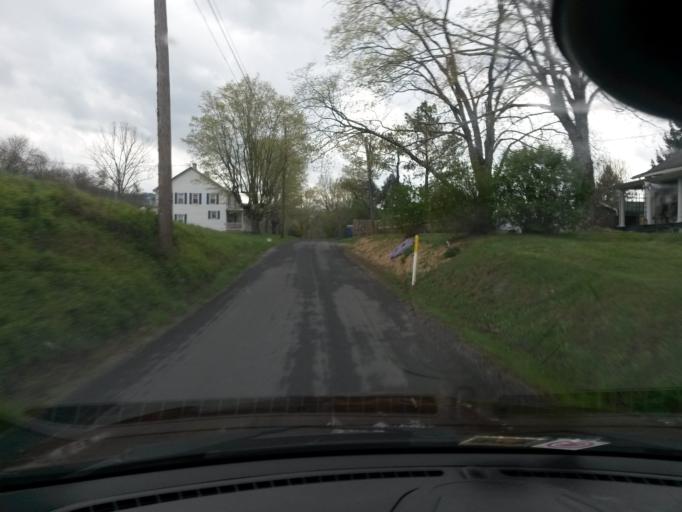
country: US
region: Virginia
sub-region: Alleghany County
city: Clifton Forge
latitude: 37.6904
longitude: -79.8098
